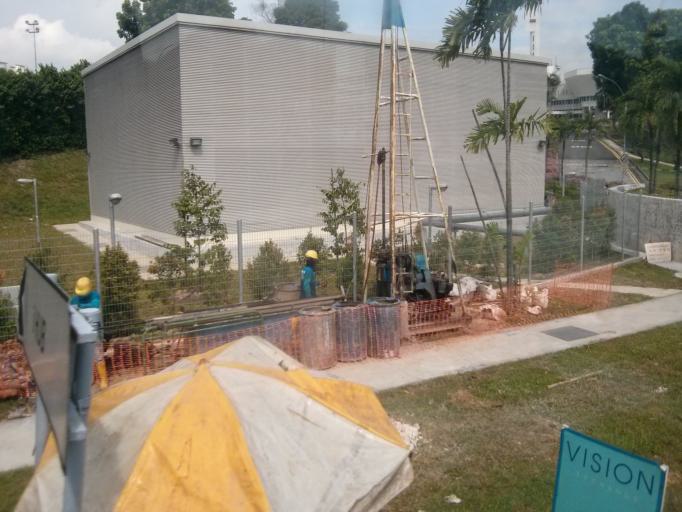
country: SG
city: Singapore
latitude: 1.3280
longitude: 103.7447
